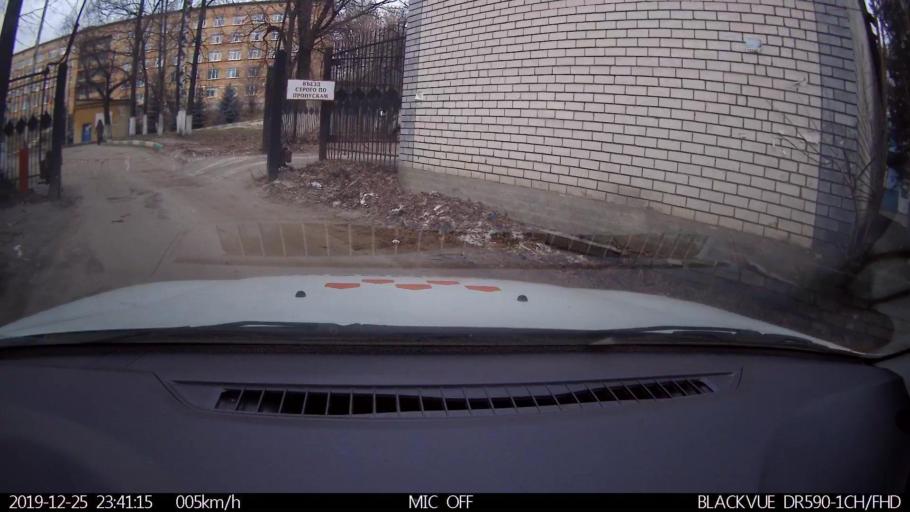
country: RU
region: Nizjnij Novgorod
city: Neklyudovo
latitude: 56.3466
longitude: 43.8622
